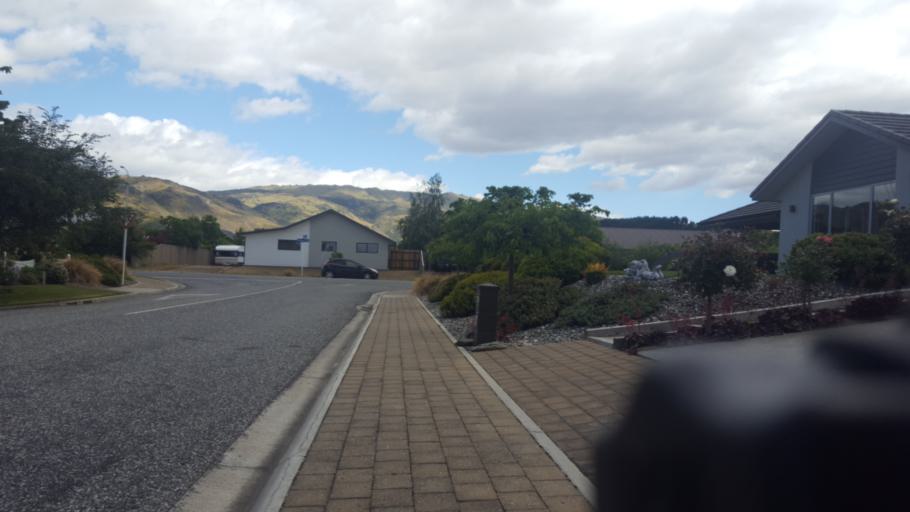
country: NZ
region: Otago
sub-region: Queenstown-Lakes District
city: Wanaka
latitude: -45.1966
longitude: 169.3328
